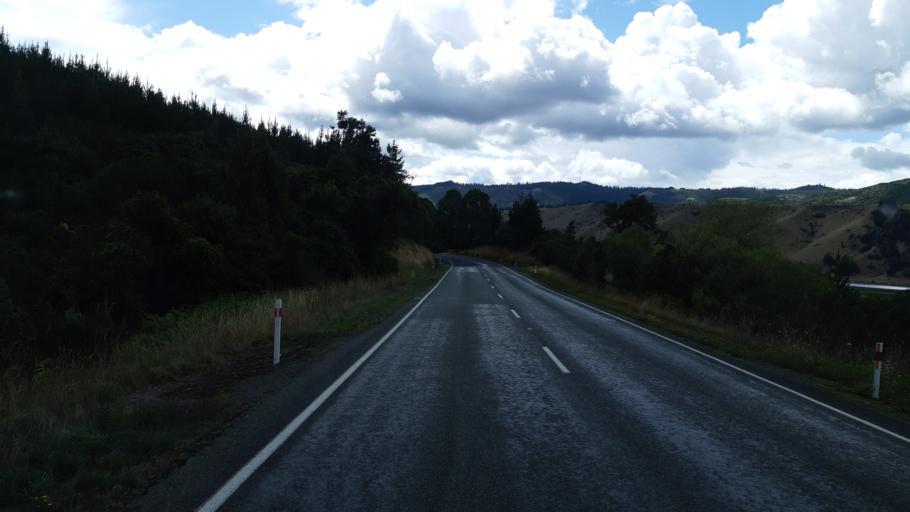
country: NZ
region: Tasman
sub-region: Tasman District
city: Wakefield
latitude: -41.5508
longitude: 172.7906
